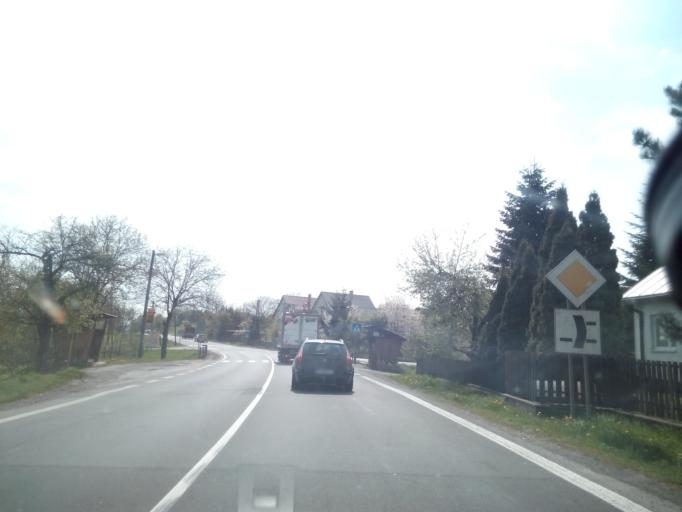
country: SK
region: Presovsky
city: Giraltovce
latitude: 49.0370
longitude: 21.4584
